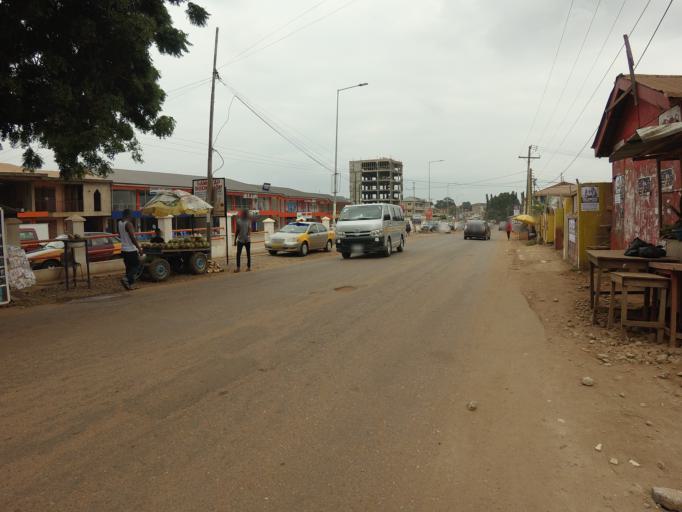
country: GH
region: Greater Accra
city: Dome
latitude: 5.6671
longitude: -0.2047
